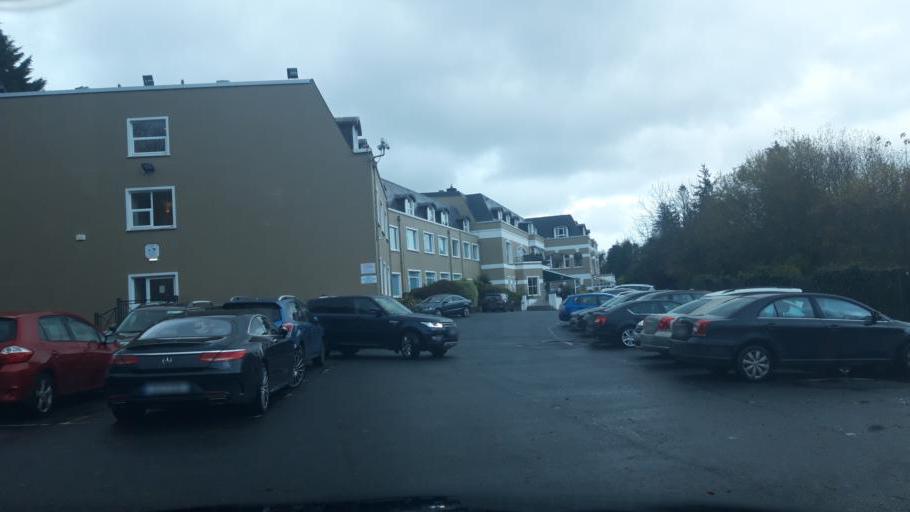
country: IE
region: Leinster
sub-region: Wicklow
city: Kilmacanoge
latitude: 53.1415
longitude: -6.1280
